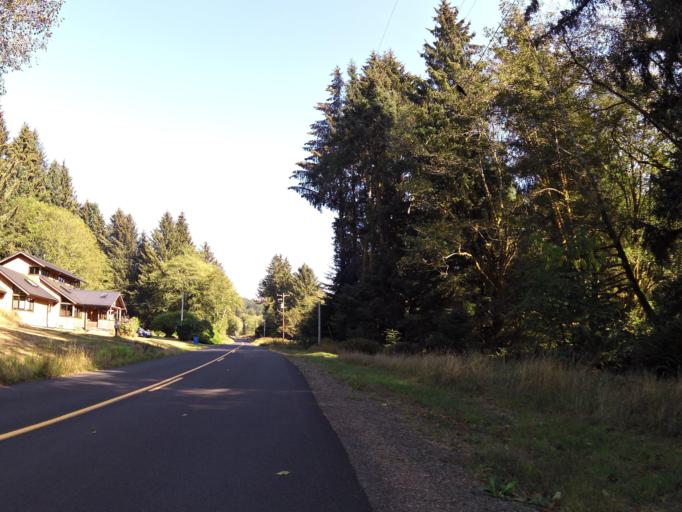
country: US
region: Oregon
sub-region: Lincoln County
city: Rose Lodge
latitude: 45.0757
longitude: -123.9346
